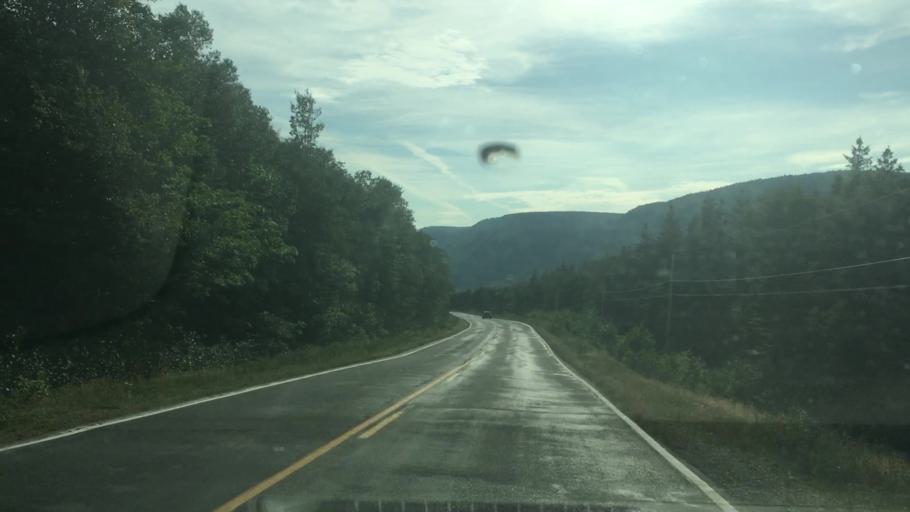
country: CA
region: Nova Scotia
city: Sydney Mines
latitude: 46.8675
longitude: -60.5560
